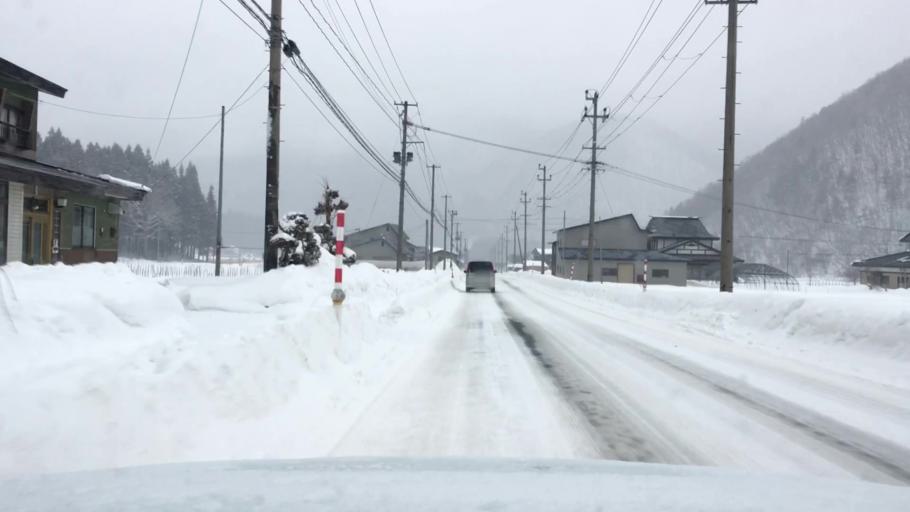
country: JP
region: Akita
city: Hanawa
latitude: 40.0741
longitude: 141.0201
